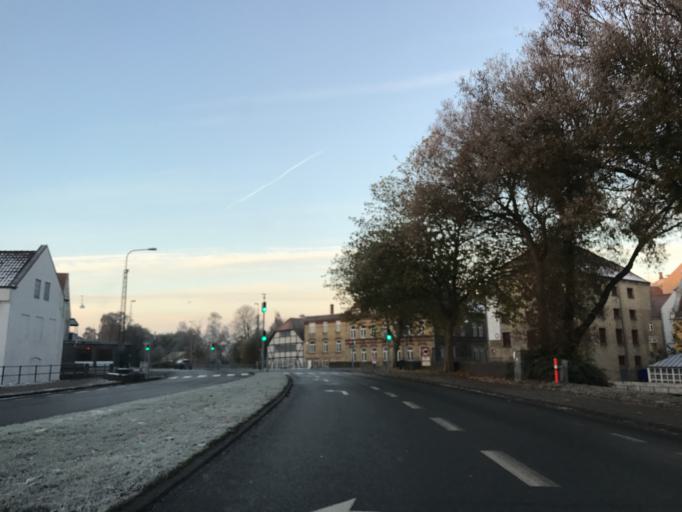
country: DK
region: South Denmark
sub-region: Haderslev Kommune
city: Haderslev
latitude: 55.2479
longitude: 9.4905
